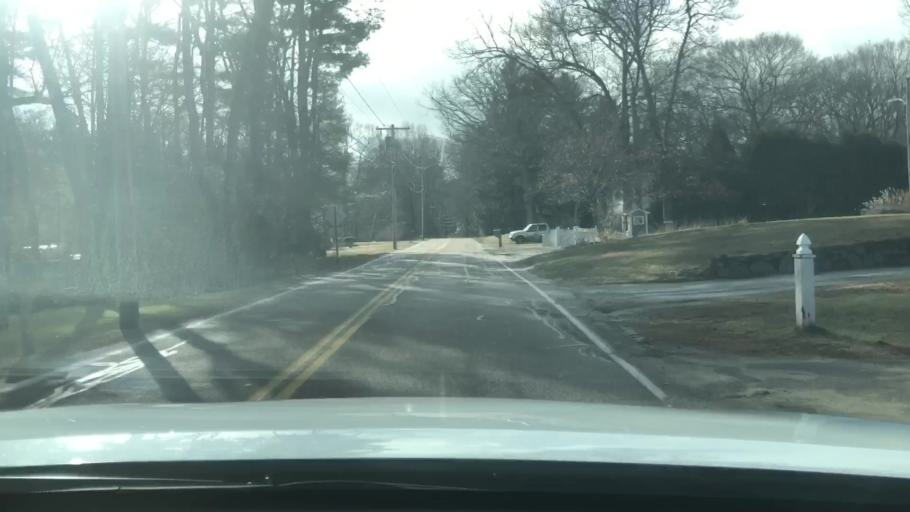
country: US
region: Massachusetts
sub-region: Worcester County
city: Blackstone
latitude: 42.0372
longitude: -71.5237
